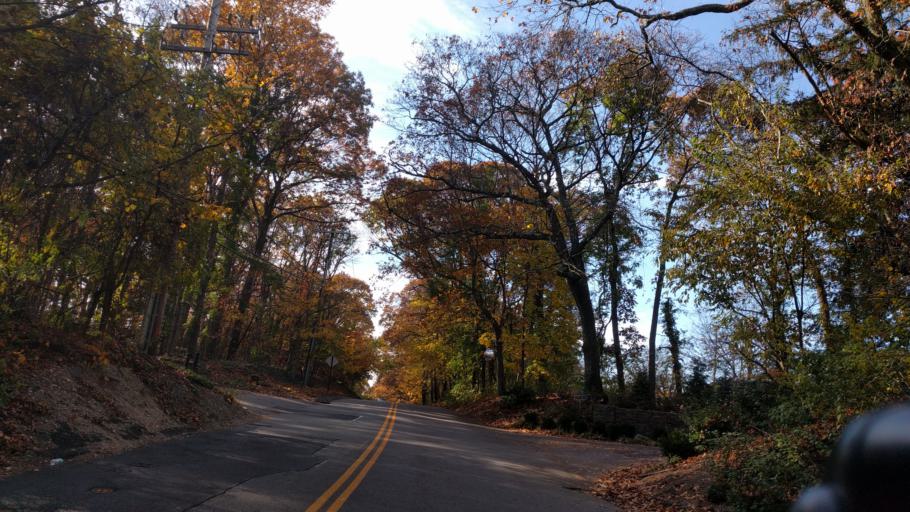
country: US
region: New York
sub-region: Nassau County
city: Oyster Bay
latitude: 40.8735
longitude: -73.5460
